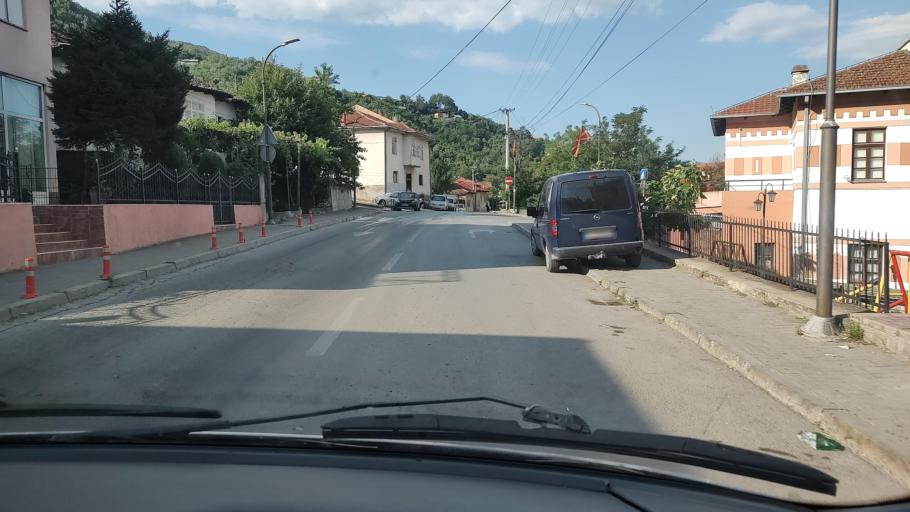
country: MK
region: Kriva Palanka
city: Kriva Palanka
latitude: 42.2019
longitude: 22.3353
